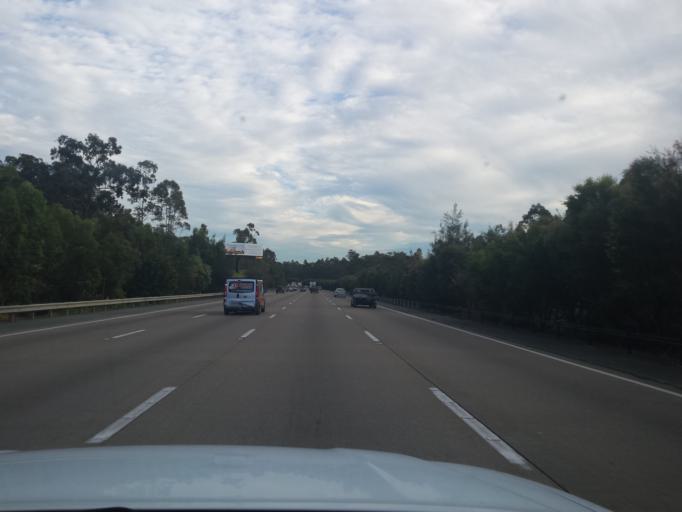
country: AU
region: Queensland
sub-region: Gold Coast
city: Oxenford
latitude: -27.8359
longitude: 153.3025
